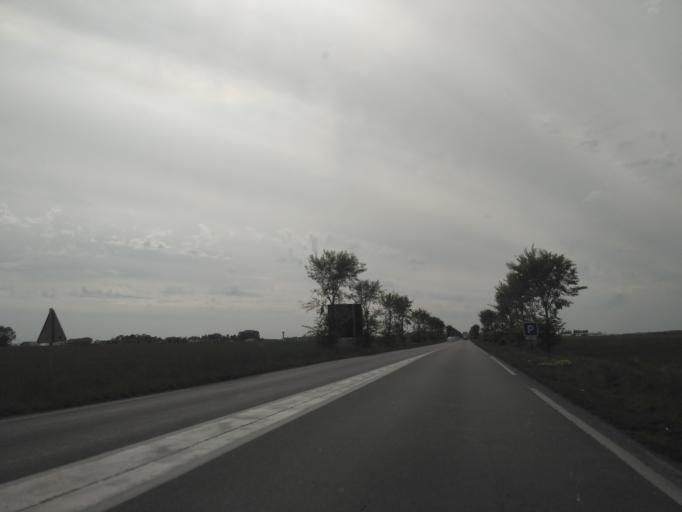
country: FR
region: Ile-de-France
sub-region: Departement de Seine-et-Marne
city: Soignolles-en-Brie
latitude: 48.6326
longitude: 2.6977
